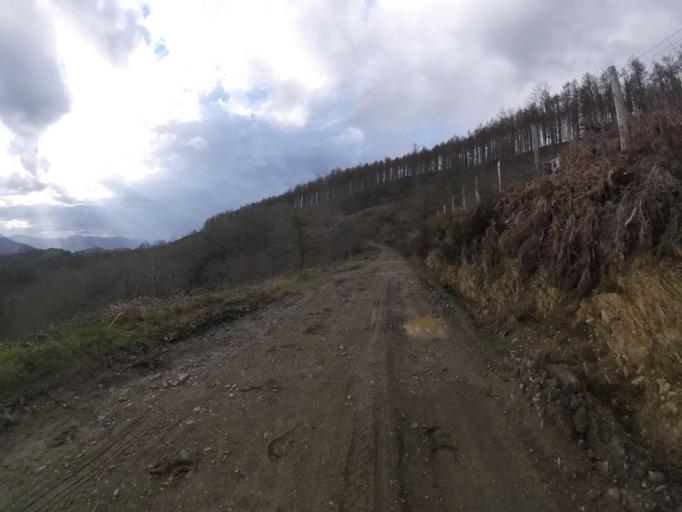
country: ES
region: Navarre
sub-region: Provincia de Navarra
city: Arano
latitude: 43.2529
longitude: -1.8789
